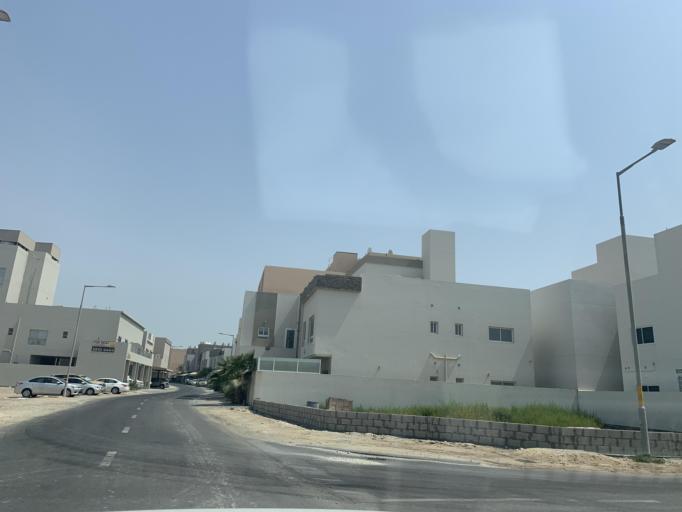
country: BH
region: Manama
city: Jidd Hafs
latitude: 26.2080
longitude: 50.5030
